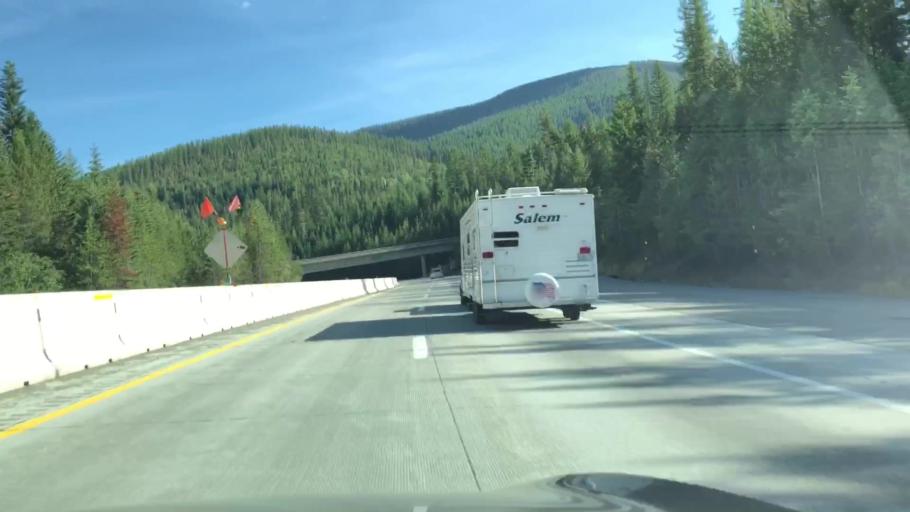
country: US
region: Idaho
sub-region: Shoshone County
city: Wallace
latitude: 47.4680
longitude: -115.7600
